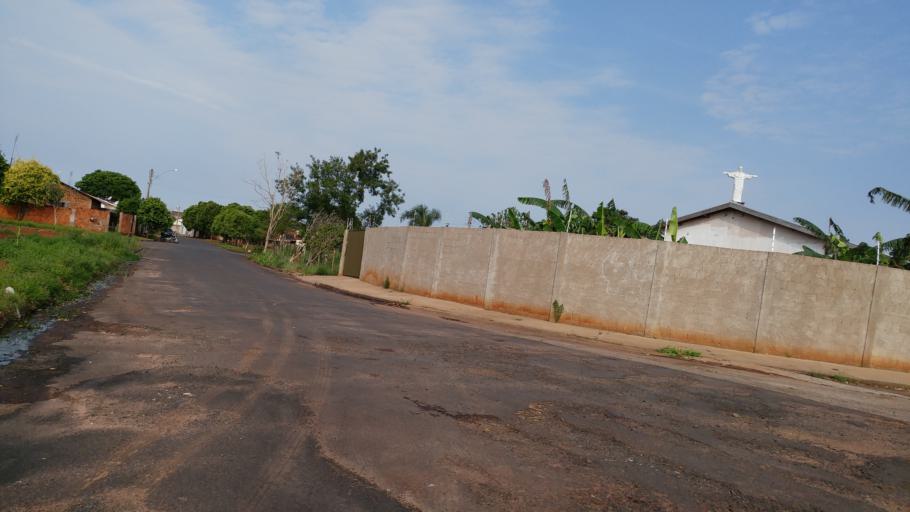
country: BR
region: Sao Paulo
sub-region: Paraguacu Paulista
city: Paraguacu Paulista
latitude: -22.4151
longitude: -50.5941
